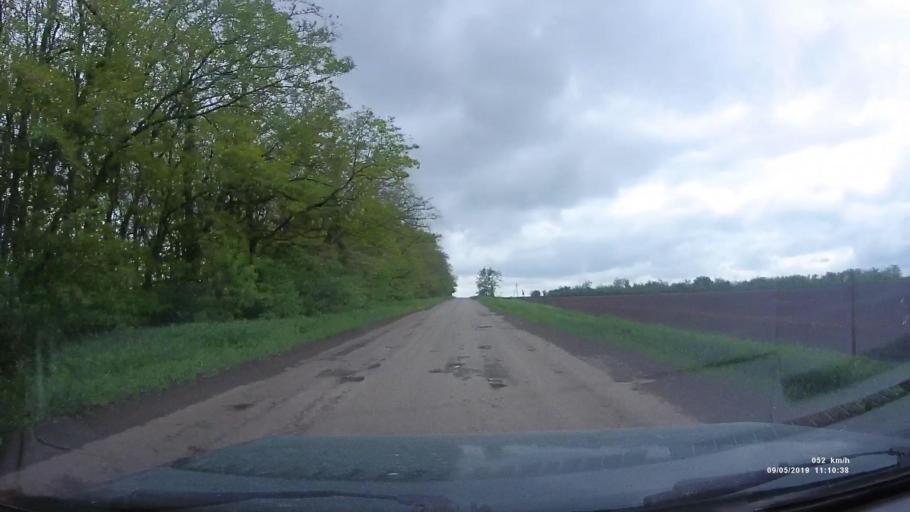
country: RU
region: Krasnodarskiy
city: Kanelovskaya
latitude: 46.7739
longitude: 39.2116
